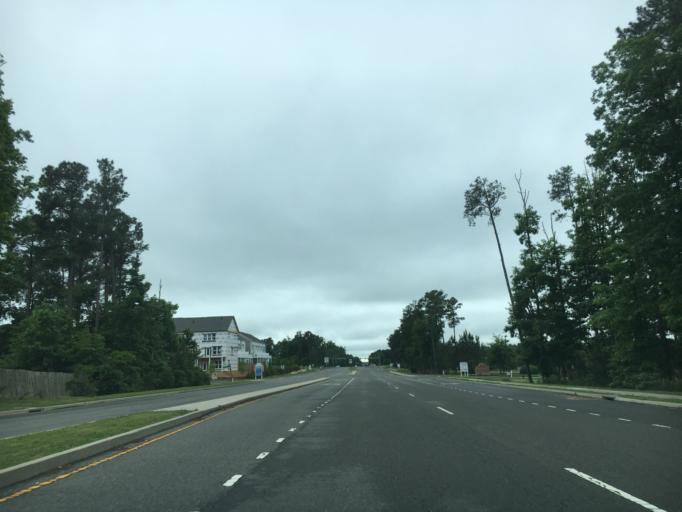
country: US
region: Virginia
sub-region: Henrico County
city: Short Pump
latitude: 37.6235
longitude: -77.6198
